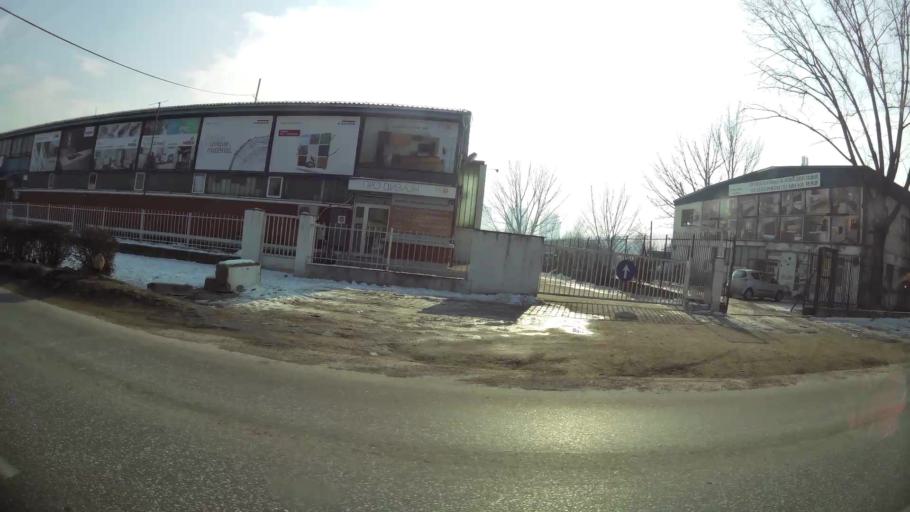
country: MK
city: Krushopek
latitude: 42.0144
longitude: 21.3842
